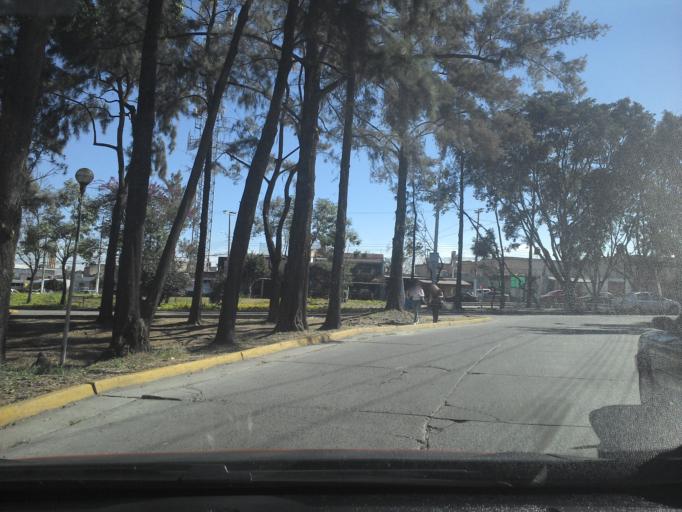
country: MX
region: Jalisco
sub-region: Zapopan
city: Zapopan
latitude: 20.7469
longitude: -103.4034
